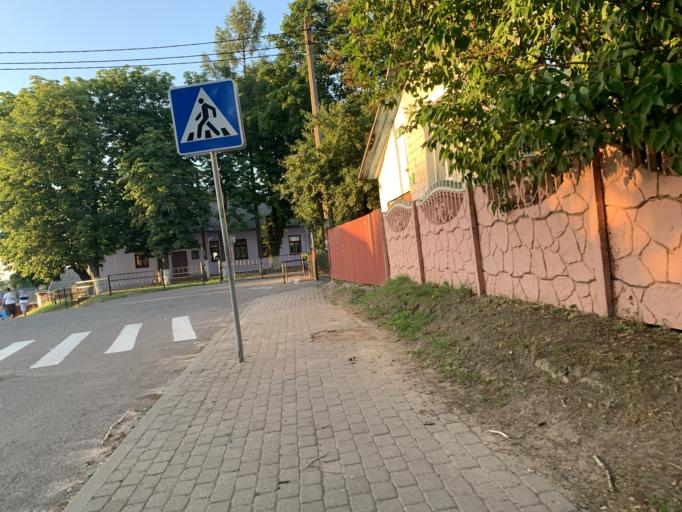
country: BY
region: Minsk
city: Nyasvizh
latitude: 53.2244
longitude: 26.6796
